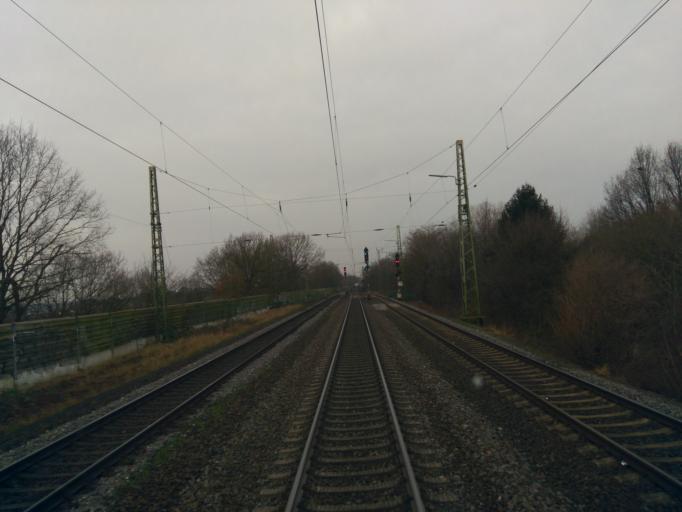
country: DE
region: Lower Saxony
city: Achim
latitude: 53.0169
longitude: 9.0251
